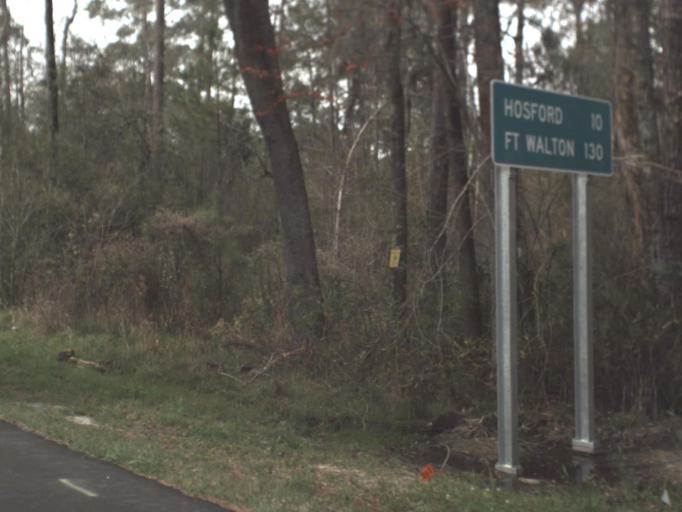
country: US
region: Florida
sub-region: Gadsden County
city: Quincy
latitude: 30.3885
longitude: -84.6360
